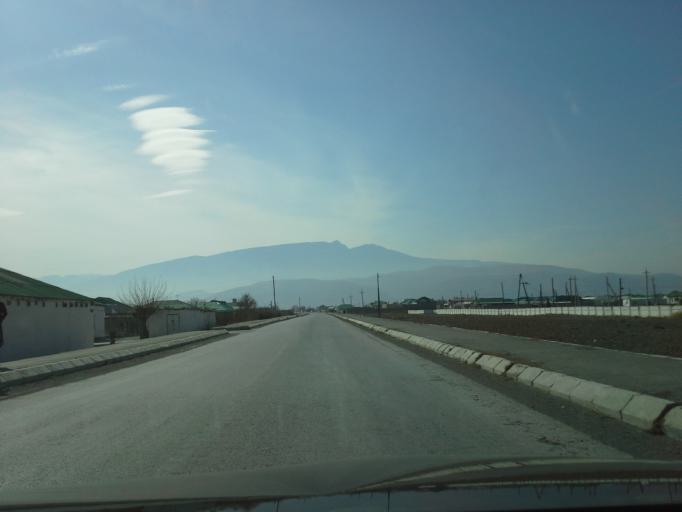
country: TM
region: Ahal
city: Abadan
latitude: 38.1070
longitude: 58.0303
